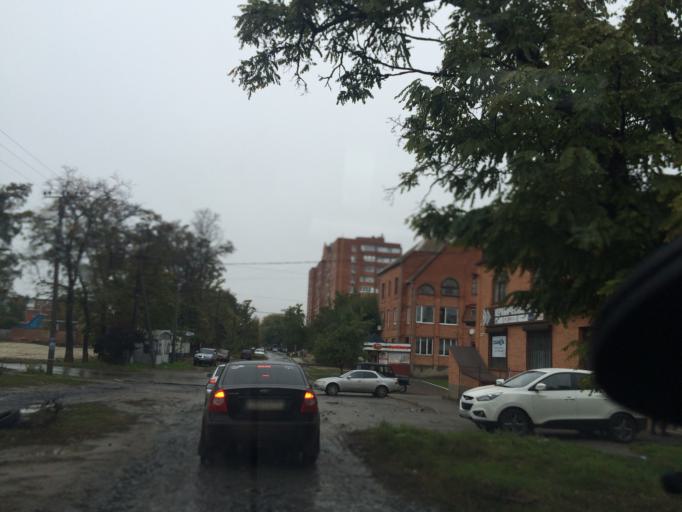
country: RU
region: Rostov
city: Azov
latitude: 47.1050
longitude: 39.4313
